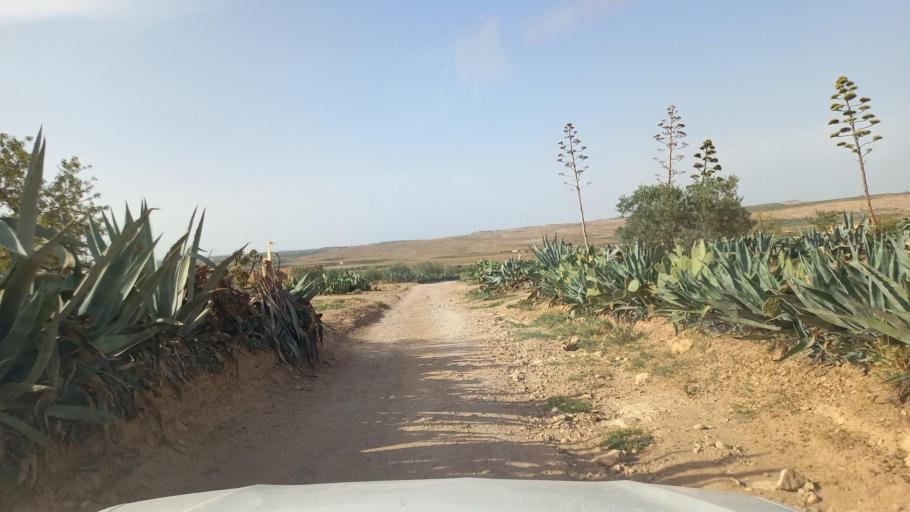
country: TN
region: Al Qasrayn
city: Kasserine
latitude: 35.3358
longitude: 8.8452
